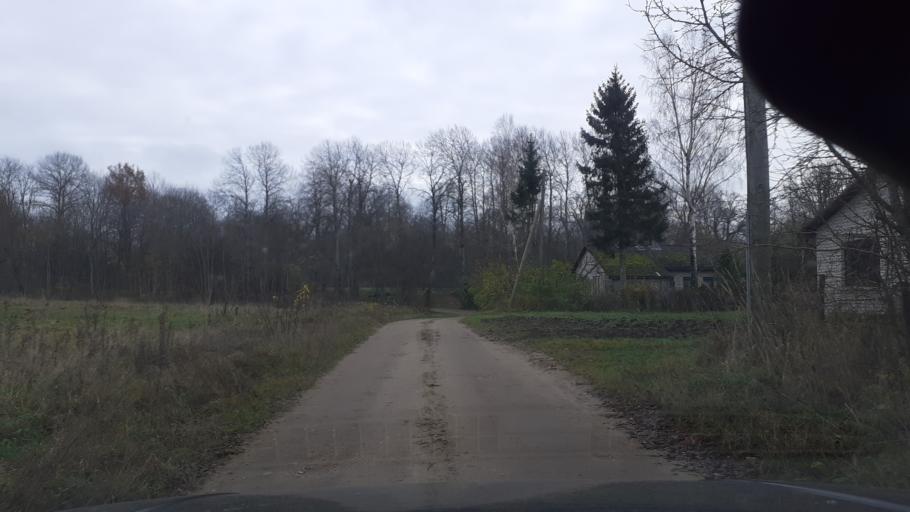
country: LV
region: Aizpute
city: Aizpute
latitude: 56.7839
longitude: 21.7502
